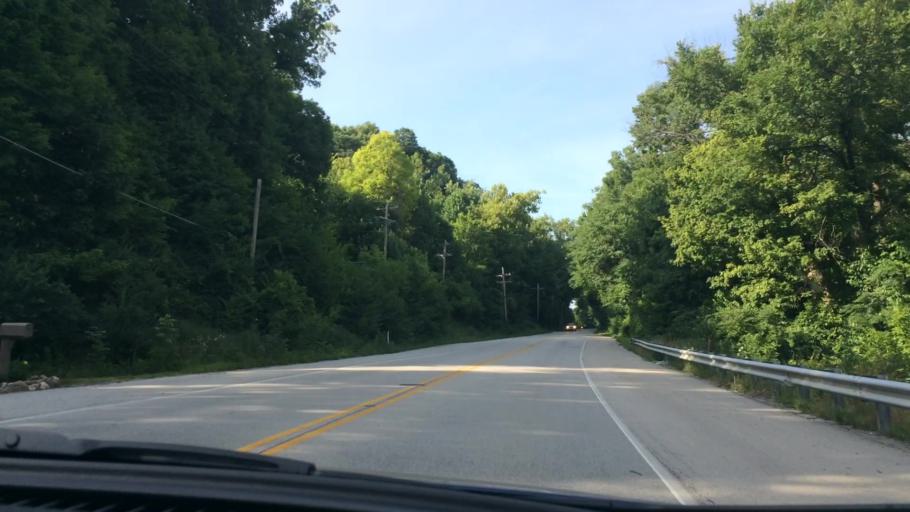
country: US
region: Indiana
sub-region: Tippecanoe County
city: West Lafayette
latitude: 40.4672
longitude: -86.8872
